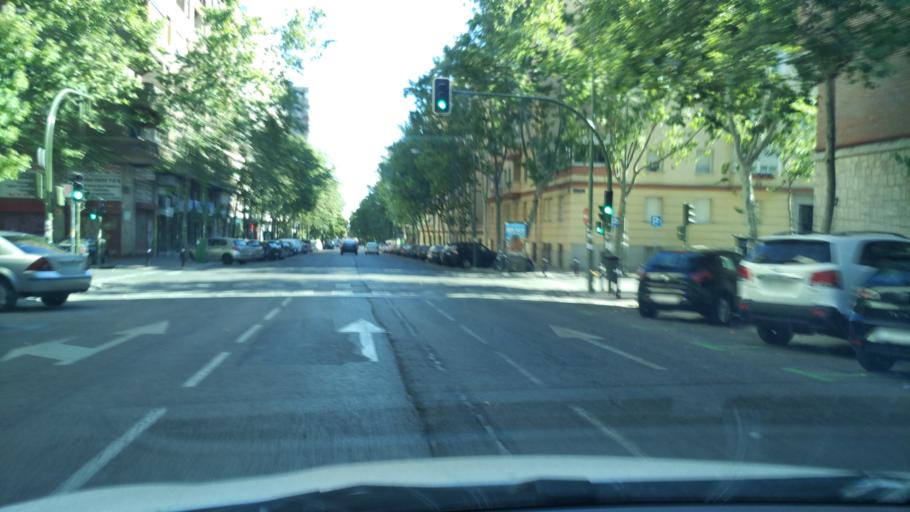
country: ES
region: Madrid
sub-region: Provincia de Madrid
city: Chamartin
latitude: 40.4555
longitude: -3.6947
